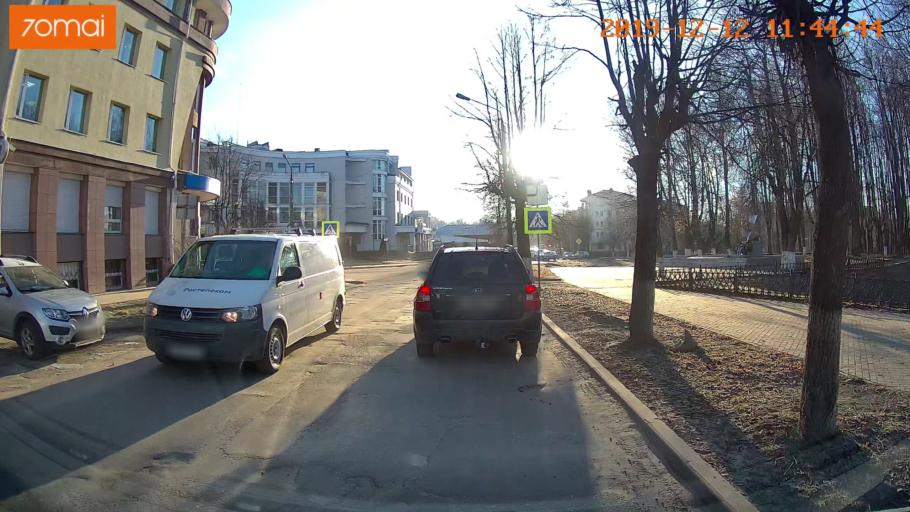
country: RU
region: Ivanovo
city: Shuya
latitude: 56.8536
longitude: 41.3749
